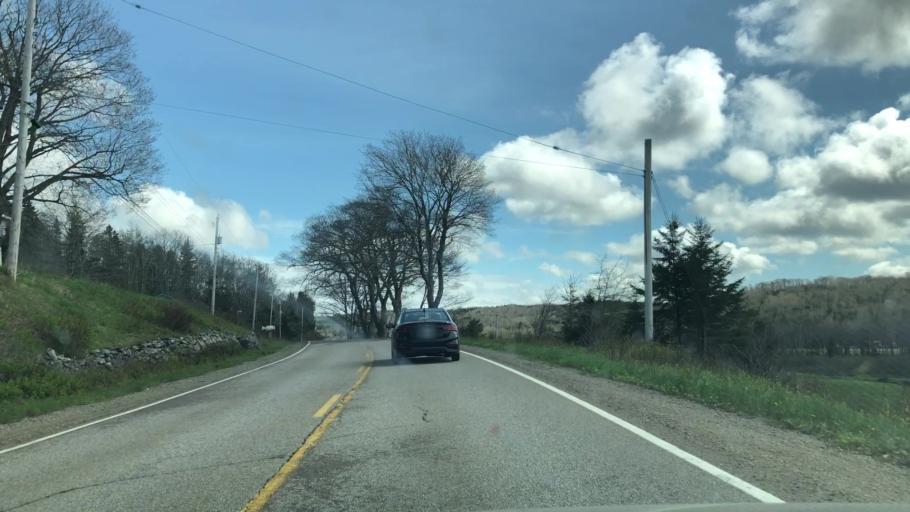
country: CA
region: Nova Scotia
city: Antigonish
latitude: 45.2018
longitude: -62.0035
